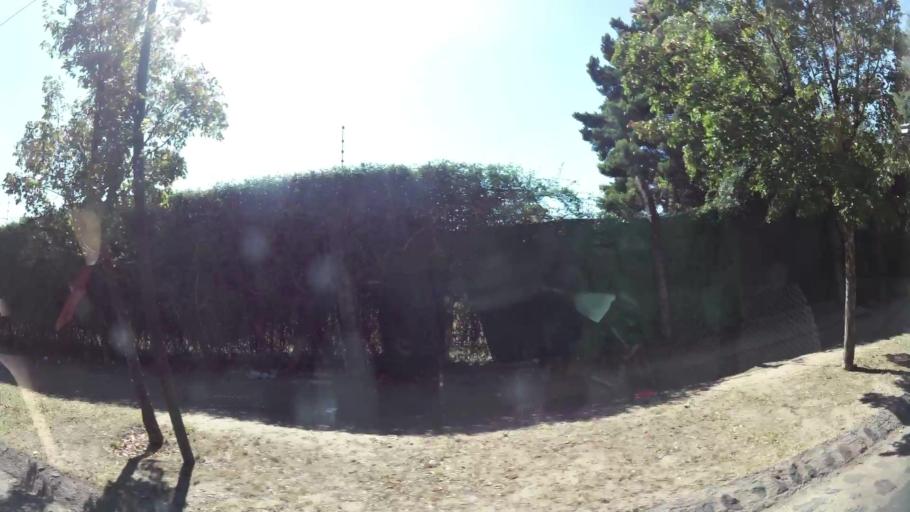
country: AR
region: Cordoba
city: Villa Allende
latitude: -31.2984
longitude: -64.2790
